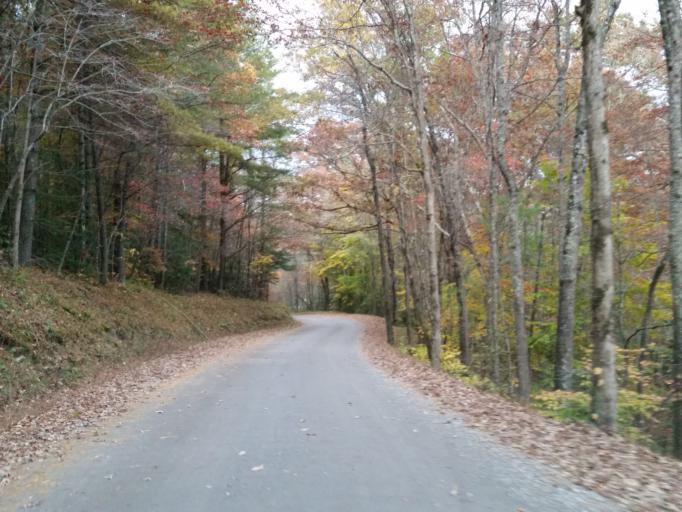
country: US
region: Georgia
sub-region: Fannin County
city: Blue Ridge
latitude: 34.7279
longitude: -84.2015
